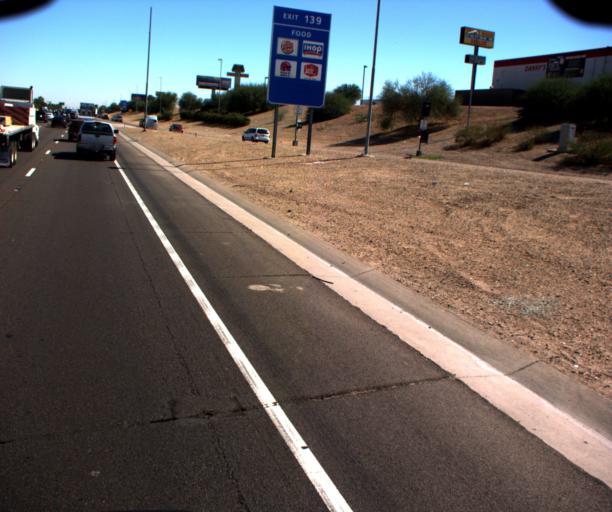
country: US
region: Arizona
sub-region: Maricopa County
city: Glendale
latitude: 33.4627
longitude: -112.1843
